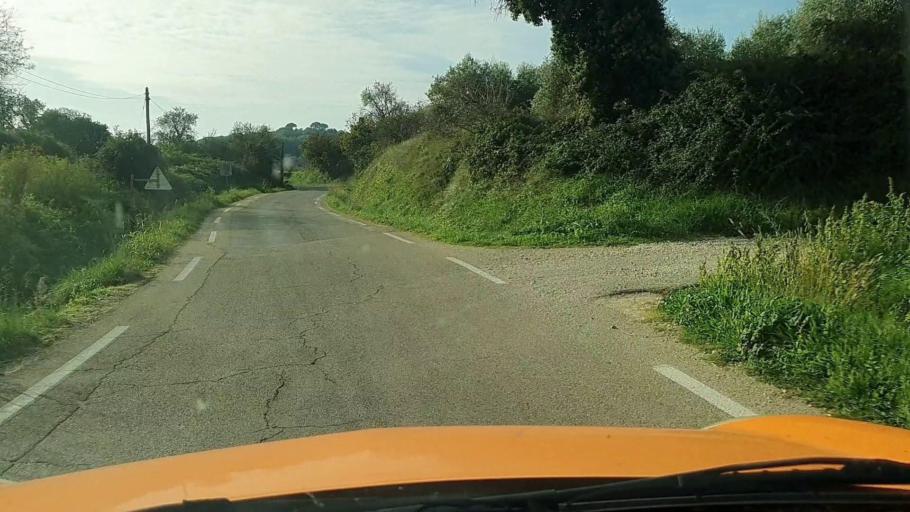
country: FR
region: Languedoc-Roussillon
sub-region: Departement du Gard
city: Generac
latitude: 43.7253
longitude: 4.3425
